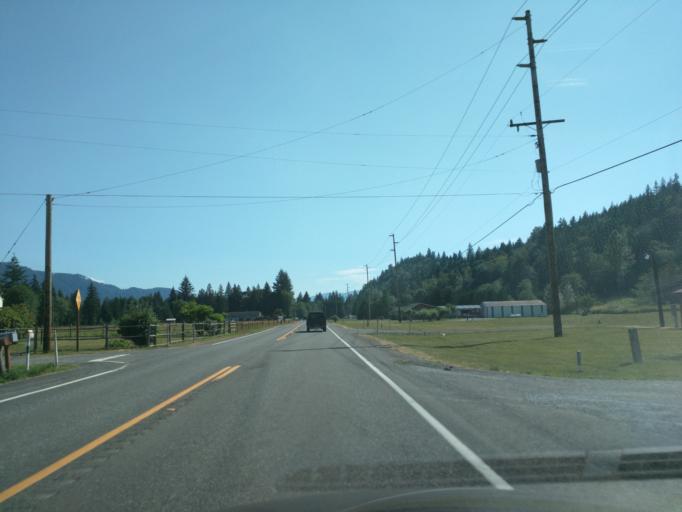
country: US
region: Washington
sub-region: Whatcom County
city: Peaceful Valley
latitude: 48.8434
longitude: -122.1646
